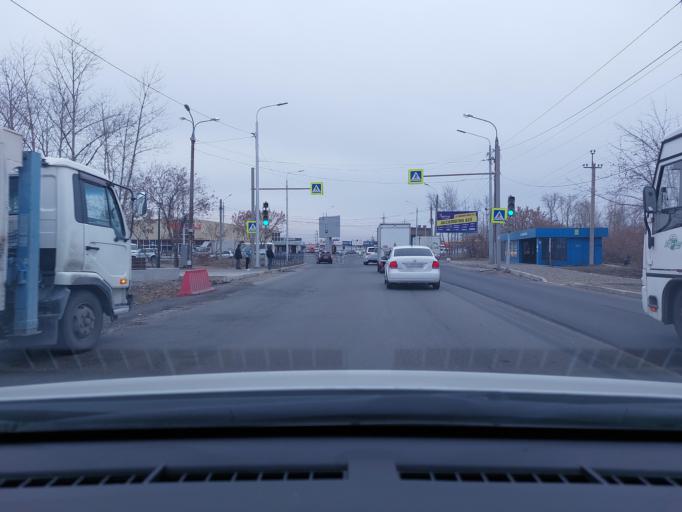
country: RU
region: Irkutsk
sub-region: Irkutskiy Rayon
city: Irkutsk
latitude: 52.3294
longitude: 104.2331
